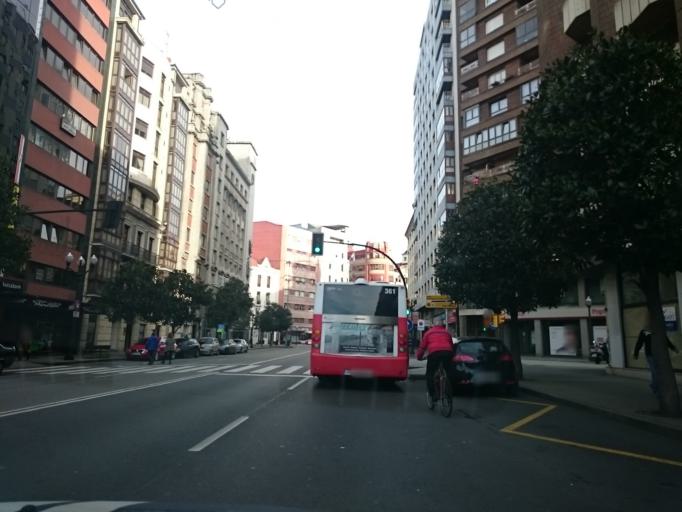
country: ES
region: Asturias
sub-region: Province of Asturias
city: Gijon
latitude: 43.5440
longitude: -5.6452
